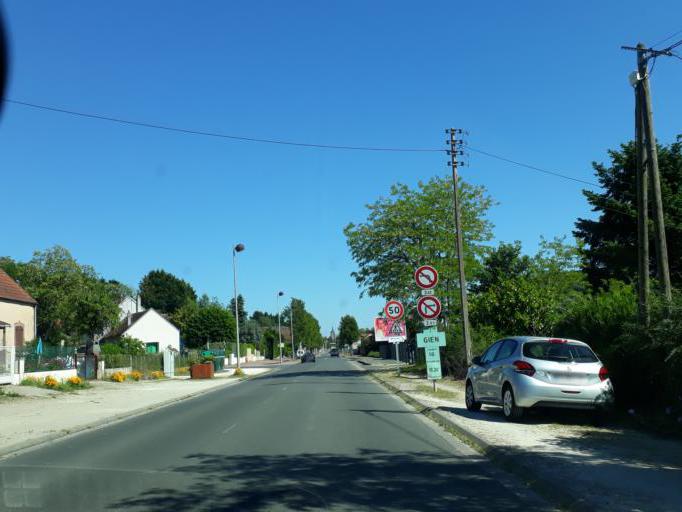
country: FR
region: Centre
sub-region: Departement du Loiret
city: Gien
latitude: 47.6957
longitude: 2.6118
